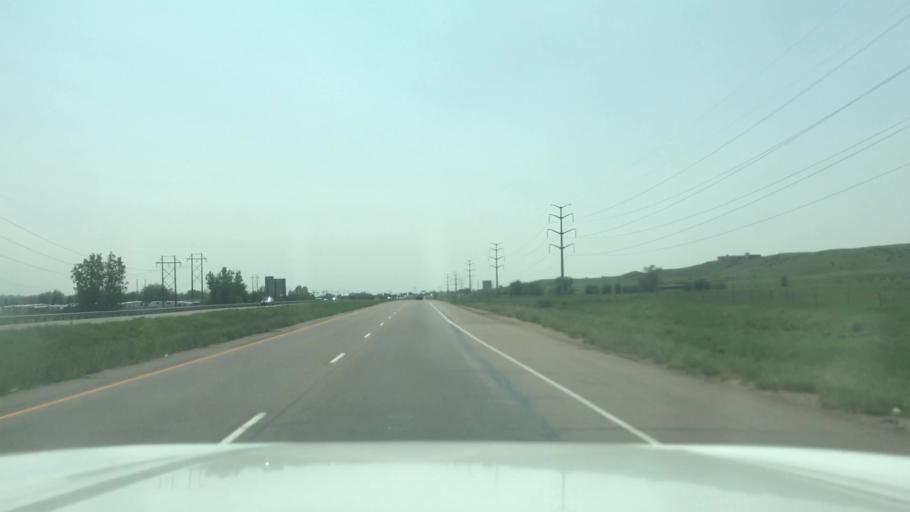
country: US
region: Colorado
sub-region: El Paso County
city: Security-Widefield
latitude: 38.7176
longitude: -104.7280
